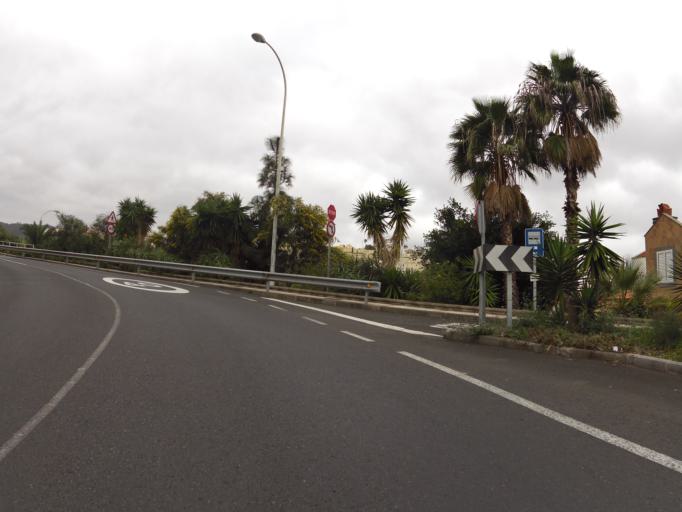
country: ES
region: Canary Islands
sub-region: Provincia de Las Palmas
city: Arucas
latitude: 28.0953
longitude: -15.4962
